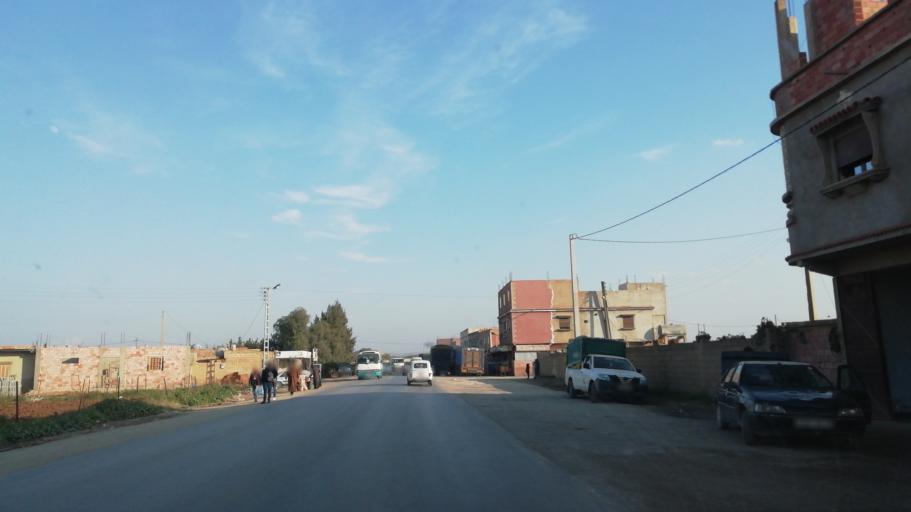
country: DZ
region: Relizane
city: Djidiouia
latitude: 35.8966
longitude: 0.6922
